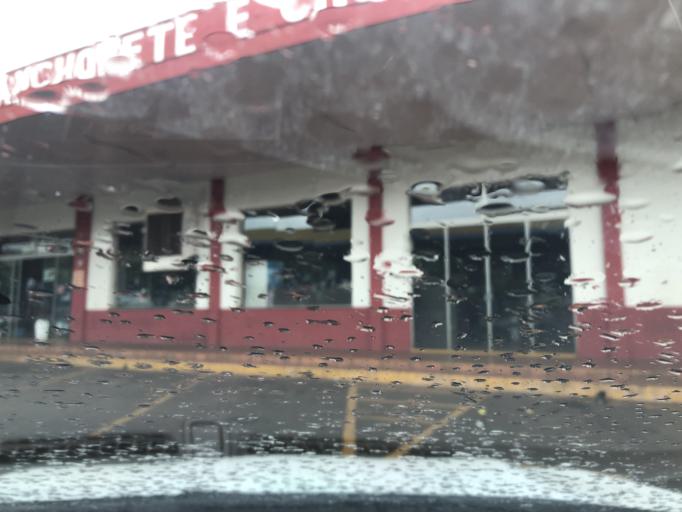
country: BR
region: Sao Paulo
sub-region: Ituverava
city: Ituverava
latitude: -20.3495
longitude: -47.8139
